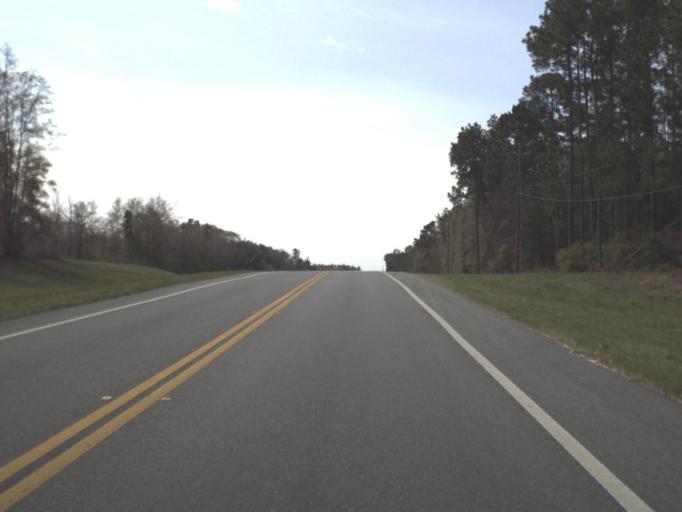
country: US
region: Florida
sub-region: Holmes County
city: Bonifay
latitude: 30.7441
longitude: -85.6852
